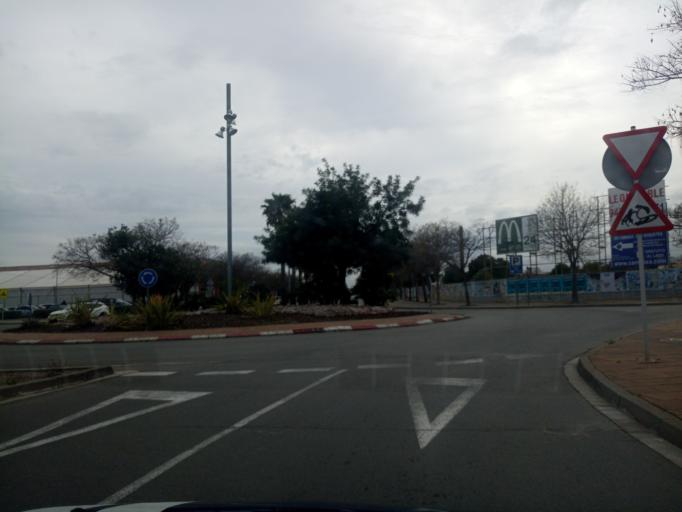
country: ES
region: Catalonia
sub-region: Provincia de Barcelona
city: Vilanova i la Geltru
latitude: 41.2278
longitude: 1.7608
